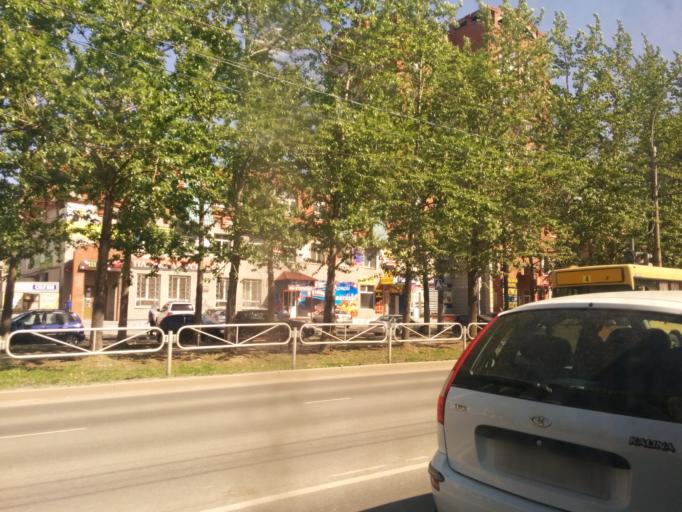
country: RU
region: Perm
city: Perm
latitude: 58.0010
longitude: 56.2868
